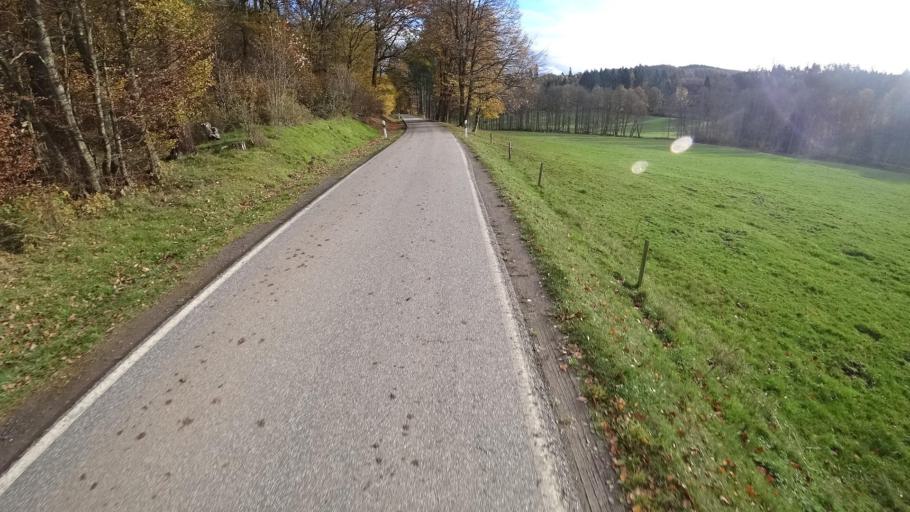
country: DE
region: Rheinland-Pfalz
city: Sierscheid
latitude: 50.4767
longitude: 6.9161
